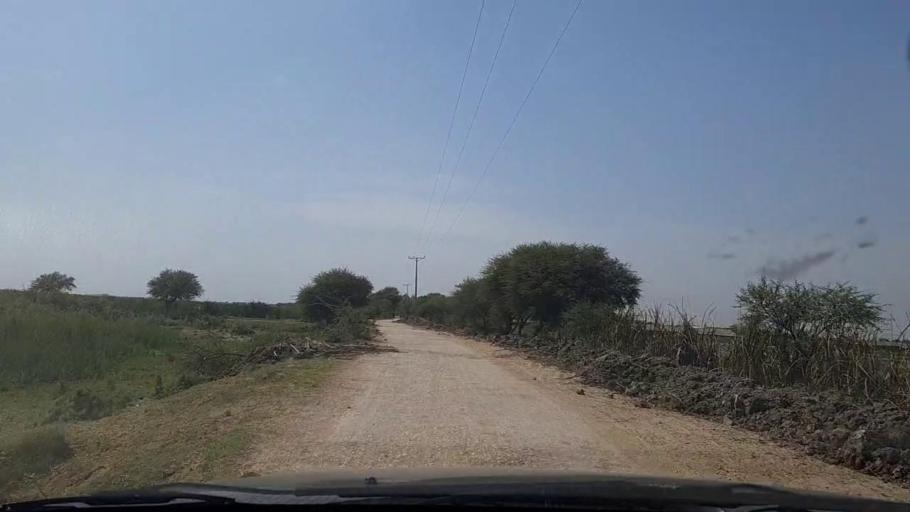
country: PK
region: Sindh
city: Mirpur Batoro
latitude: 24.6096
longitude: 68.2424
